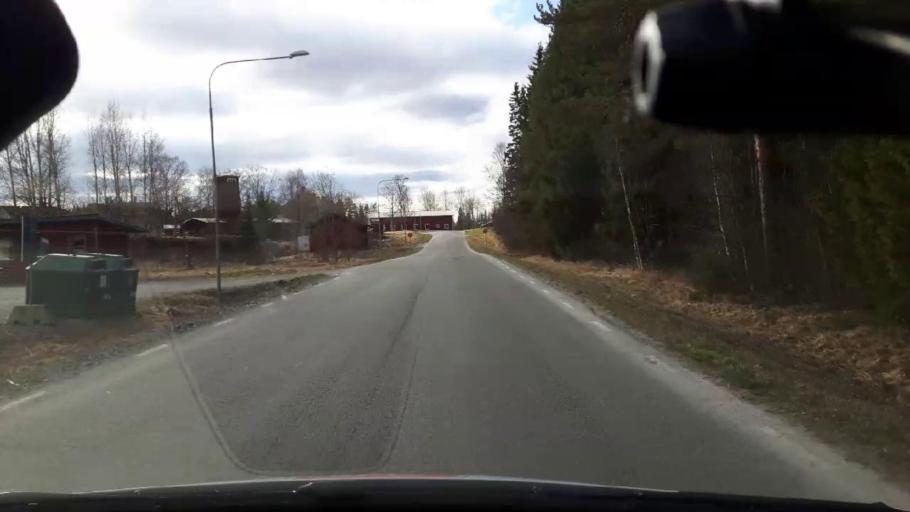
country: SE
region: Jaemtland
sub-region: OEstersunds Kommun
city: Ostersund
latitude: 62.9937
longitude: 14.5806
